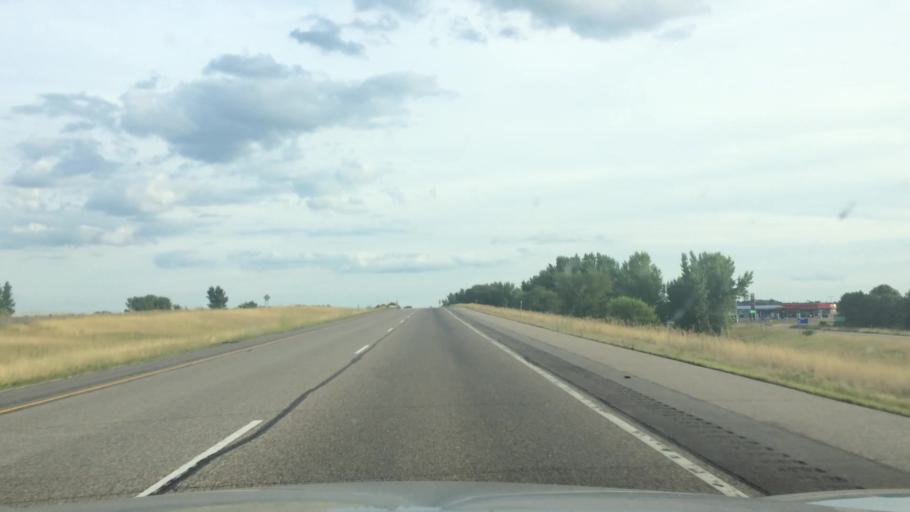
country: US
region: Wisconsin
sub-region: Portage County
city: Plover
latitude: 44.2167
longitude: -89.5248
